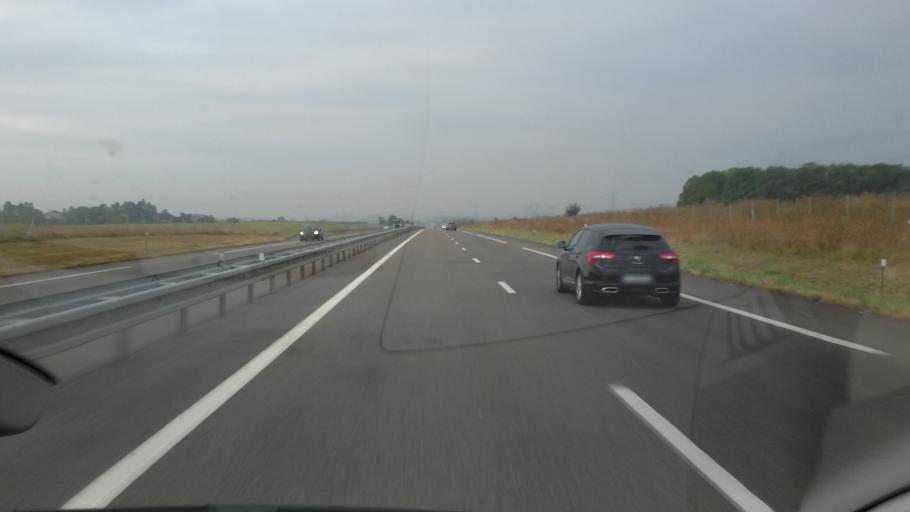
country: FR
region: Champagne-Ardenne
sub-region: Departement des Ardennes
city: Rethel
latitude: 49.5835
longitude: 4.4872
